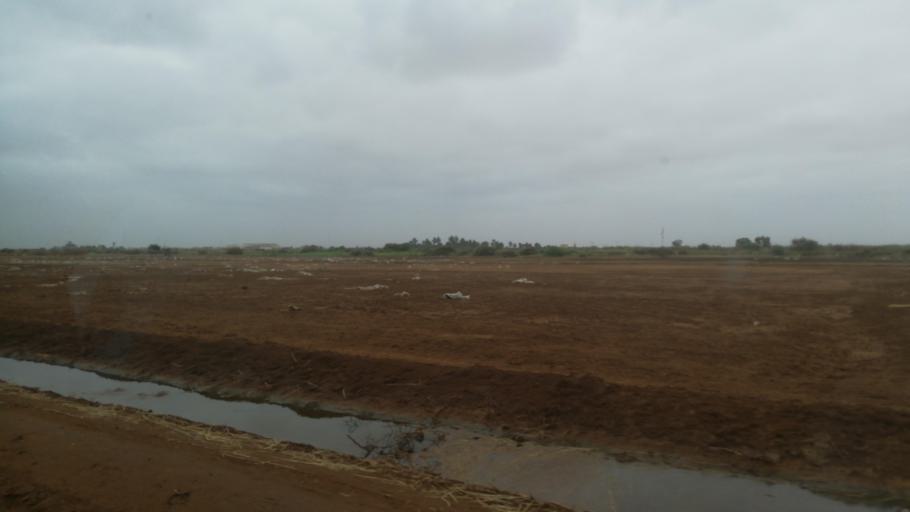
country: SN
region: Saint-Louis
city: Rosso
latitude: 16.2807
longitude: -16.1600
